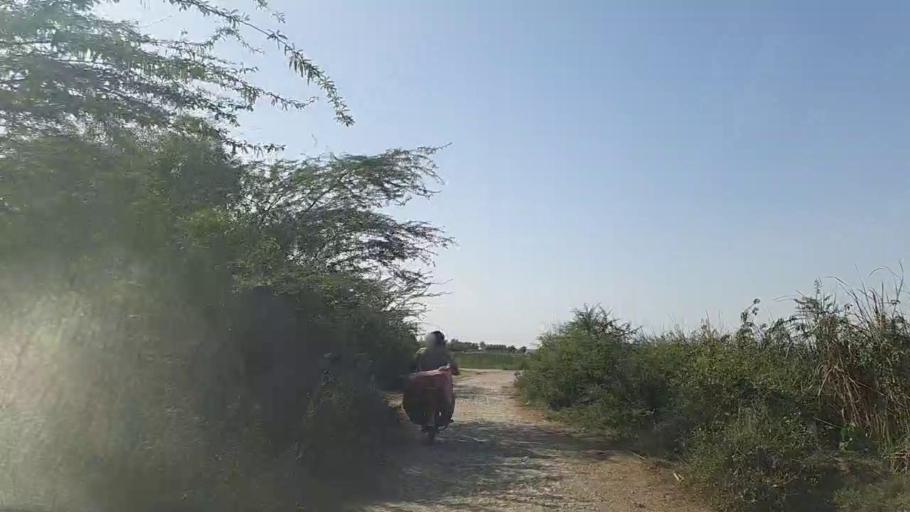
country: PK
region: Sindh
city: Thatta
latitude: 24.5914
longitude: 67.8889
